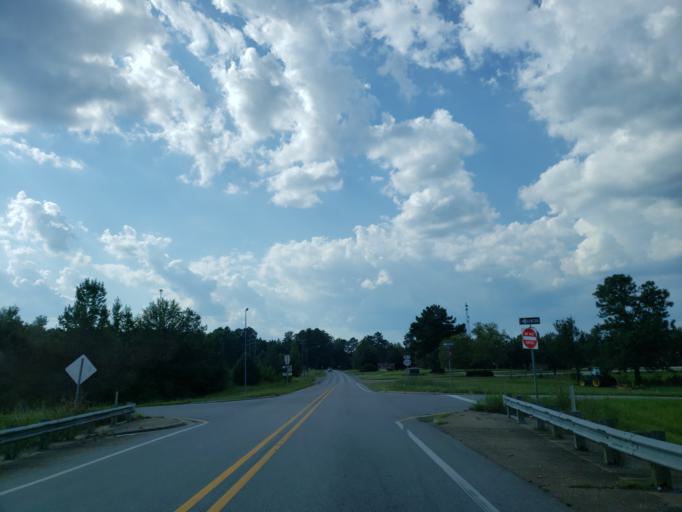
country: US
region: Mississippi
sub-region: Jones County
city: Sharon
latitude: 31.9079
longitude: -89.0156
